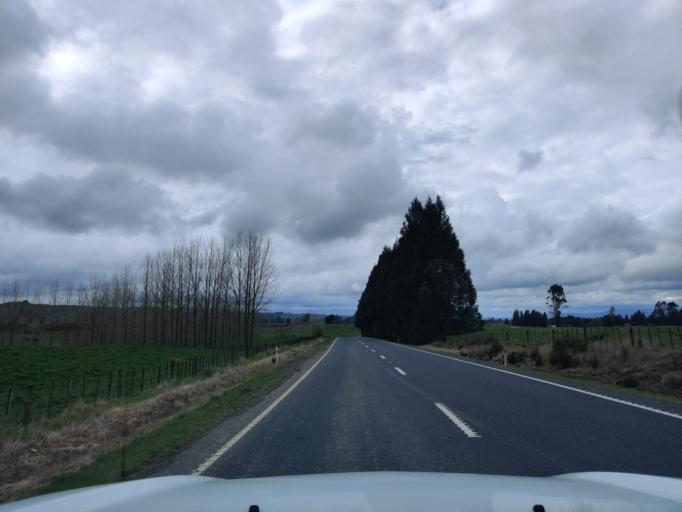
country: NZ
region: Waikato
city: Turangi
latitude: -39.0350
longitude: 175.3827
